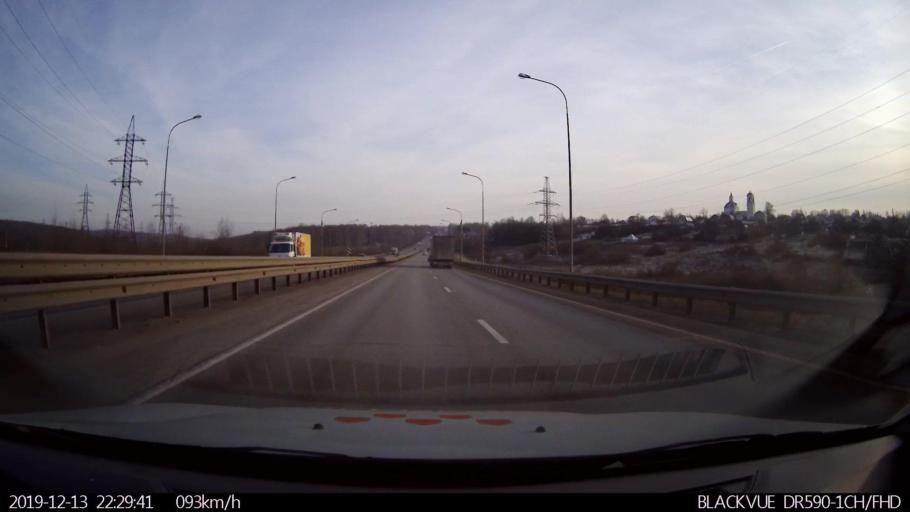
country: RU
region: Nizjnij Novgorod
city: Afonino
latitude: 56.2348
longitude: 44.0526
